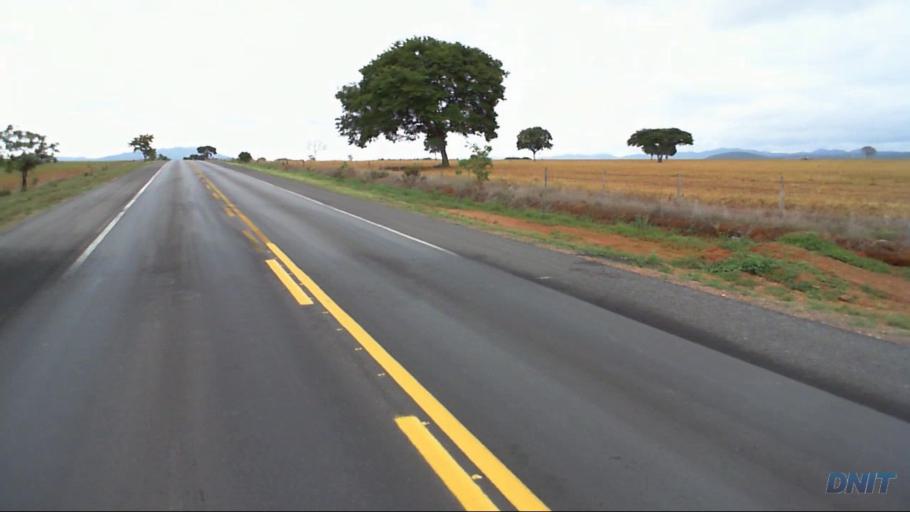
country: BR
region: Goias
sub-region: Padre Bernardo
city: Padre Bernardo
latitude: -15.2166
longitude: -48.6062
